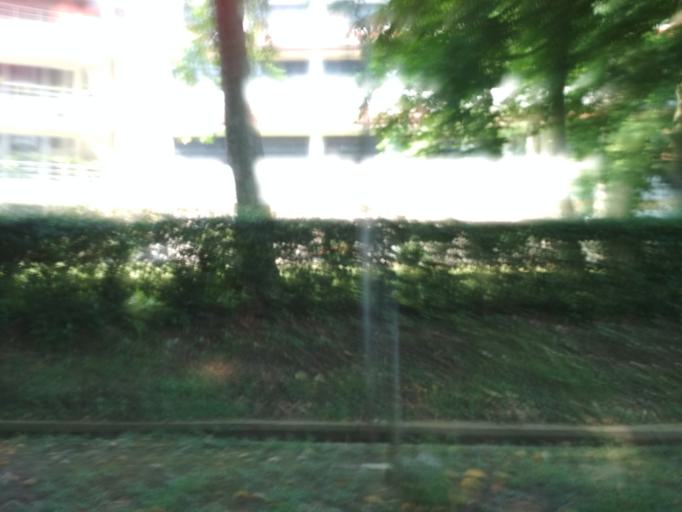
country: ID
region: West Java
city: Ciampea
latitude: -6.5568
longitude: 106.7226
